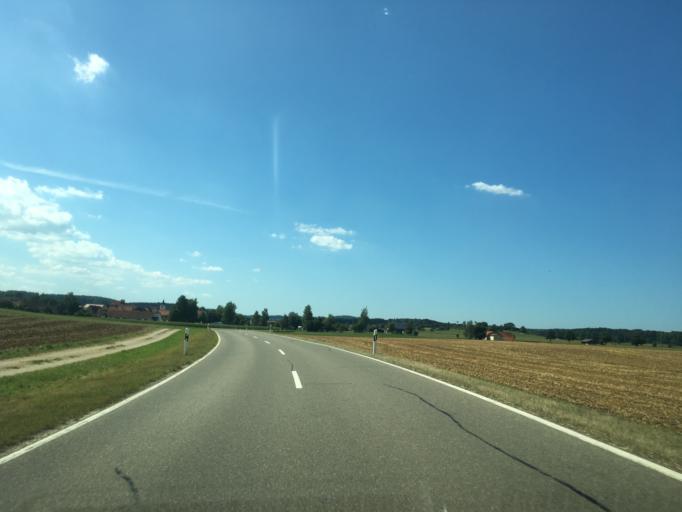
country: DE
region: Baden-Wuerttemberg
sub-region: Tuebingen Region
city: Gomadingen
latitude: 48.3503
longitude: 9.3843
